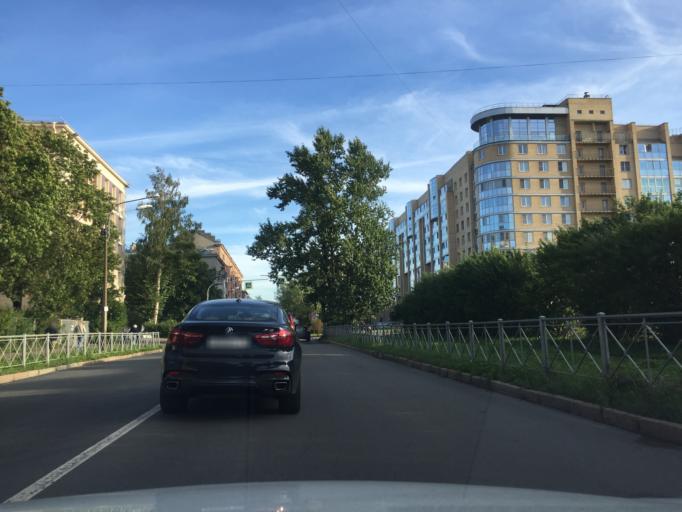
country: RU
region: St.-Petersburg
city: Admiralteisky
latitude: 59.8787
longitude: 30.3132
